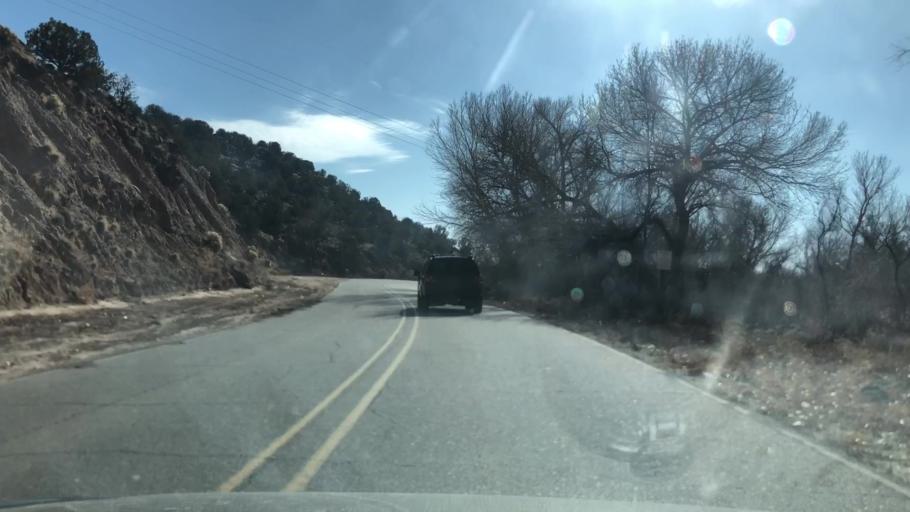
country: US
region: New Mexico
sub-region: Rio Arriba County
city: Ohkay Owingeh
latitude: 36.0870
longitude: -106.1278
